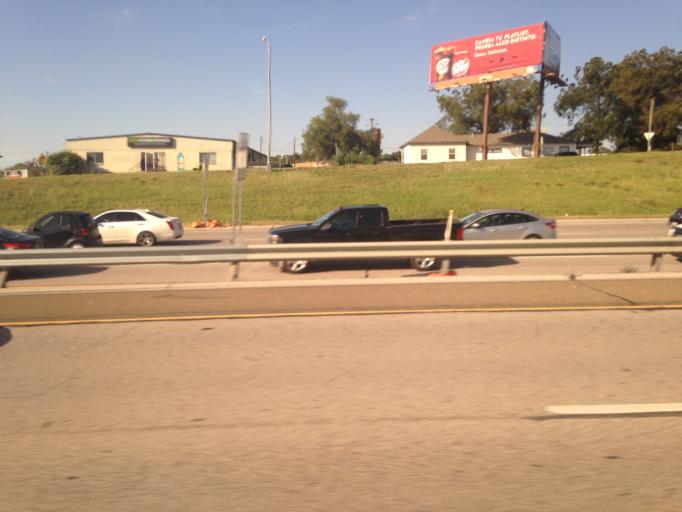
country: US
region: Texas
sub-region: Tarrant County
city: Fort Worth
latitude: 32.7673
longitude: -97.3101
